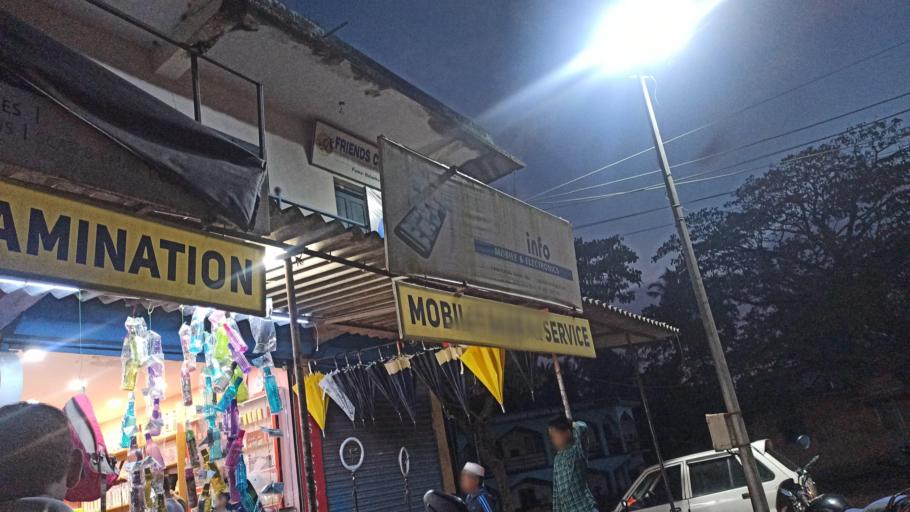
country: IN
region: Kerala
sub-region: Kasaragod District
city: Kasaragod
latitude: 12.5418
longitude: 75.0862
